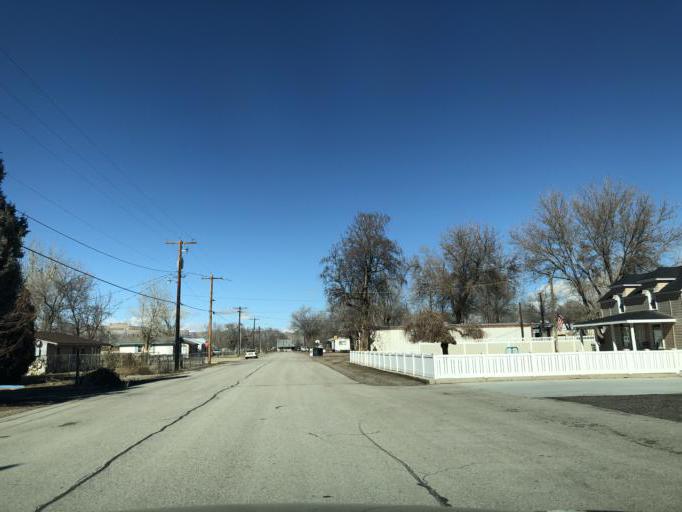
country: US
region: Utah
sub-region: Carbon County
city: East Carbon City
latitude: 38.9878
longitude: -110.1576
